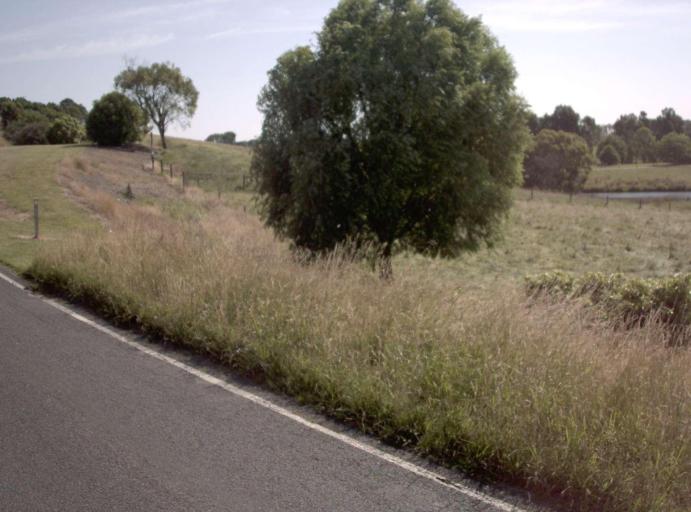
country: AU
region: Victoria
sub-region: Baw Baw
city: Warragul
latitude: -38.3173
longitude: 145.7720
